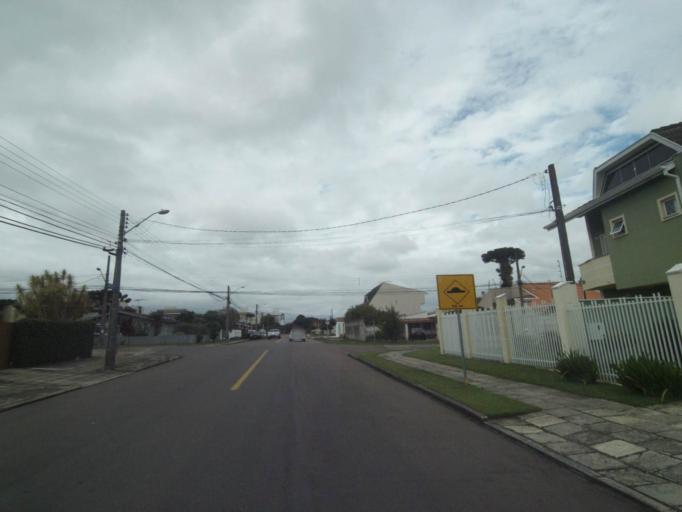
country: BR
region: Parana
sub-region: Curitiba
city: Curitiba
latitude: -25.4971
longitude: -49.2926
